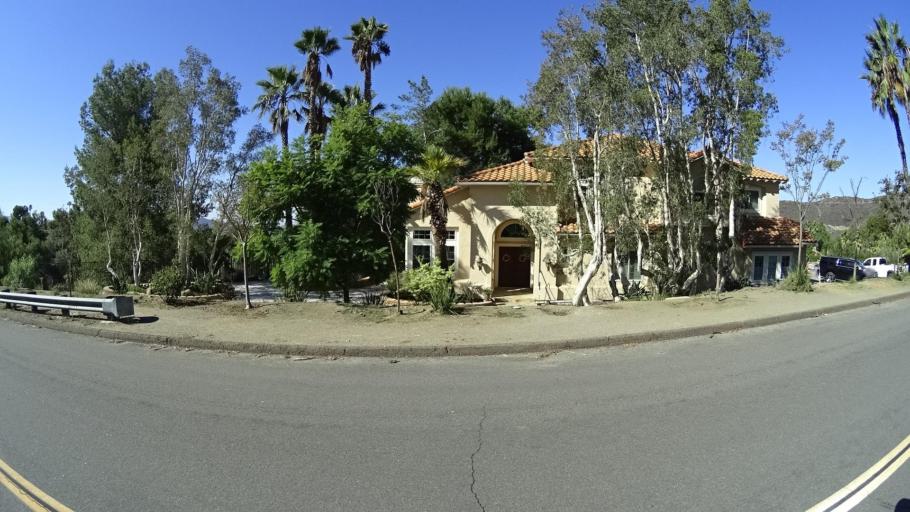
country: US
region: California
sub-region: San Diego County
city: Jamul
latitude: 32.7375
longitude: -116.8543
